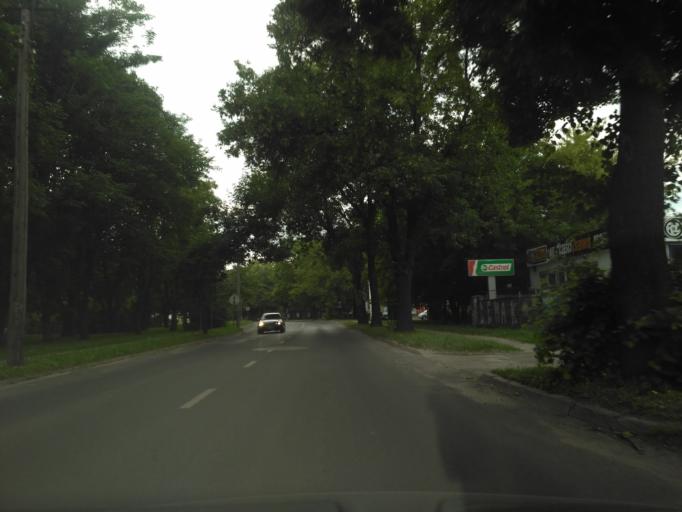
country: PL
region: Lublin Voivodeship
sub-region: Chelm
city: Chelm
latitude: 51.1390
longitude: 23.4848
